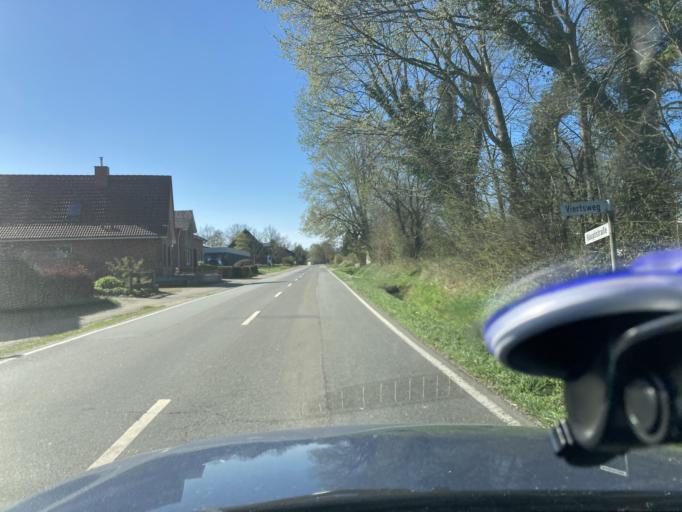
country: DE
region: Schleswig-Holstein
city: Odderade
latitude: 54.1429
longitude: 9.1914
